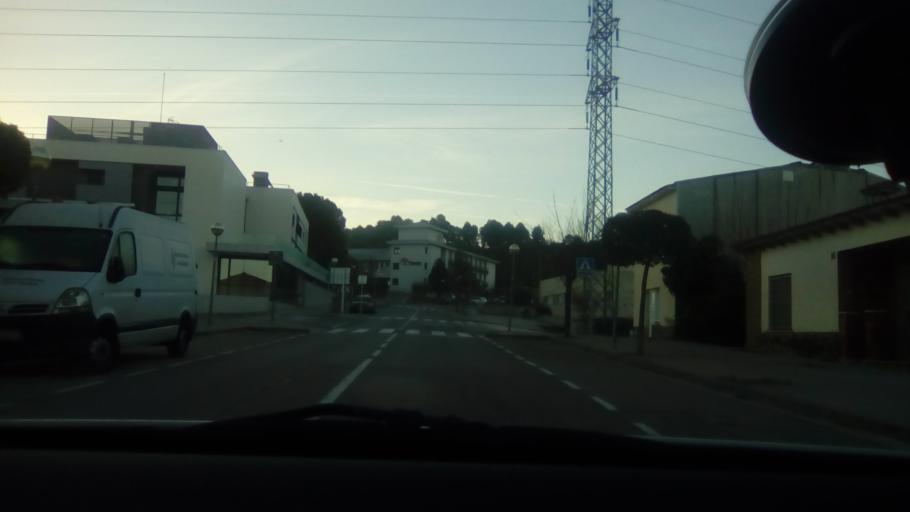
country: ES
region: Catalonia
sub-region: Provincia de Barcelona
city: Navarcles
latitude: 41.7496
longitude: 1.9085
